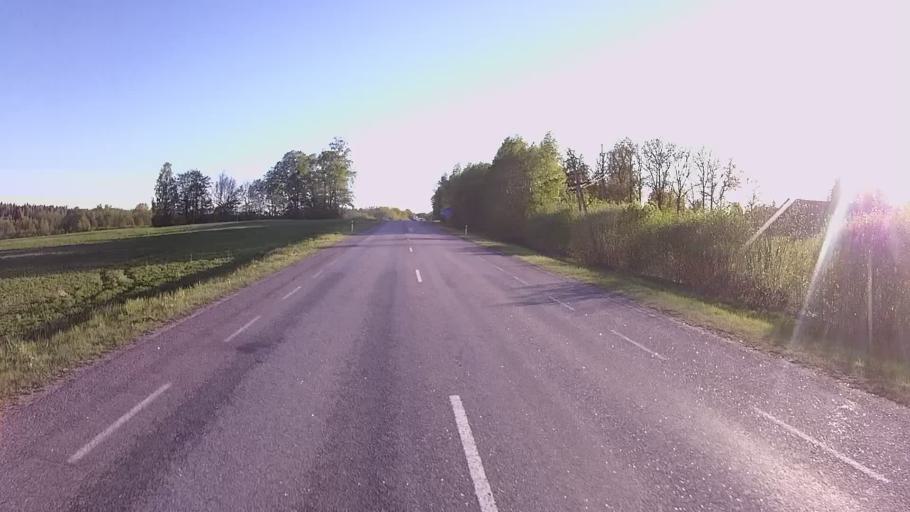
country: EE
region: Viljandimaa
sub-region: Viiratsi vald
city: Viiratsi
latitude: 58.4095
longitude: 25.6735
